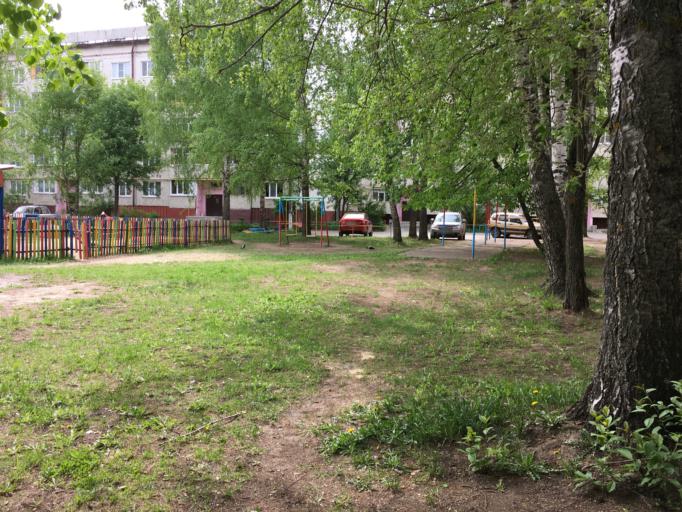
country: RU
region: Mariy-El
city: Yoshkar-Ola
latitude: 56.6460
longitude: 47.8582
